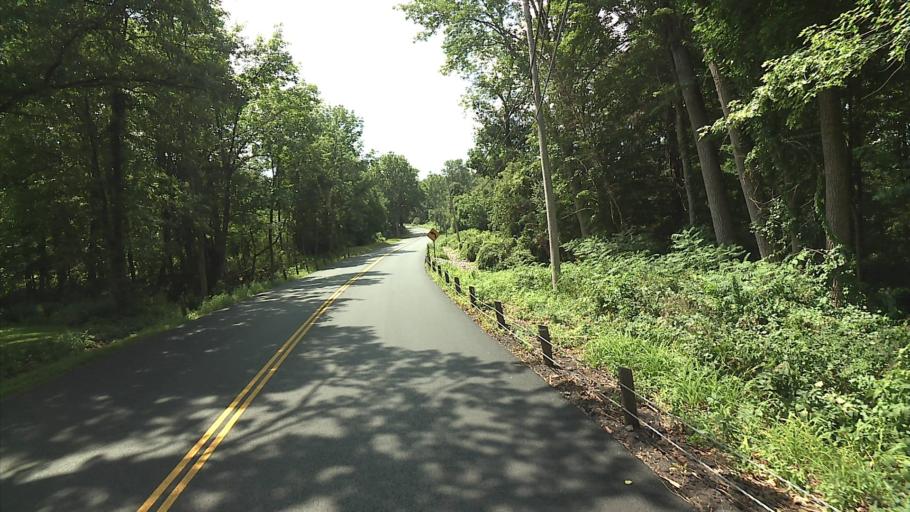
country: US
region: Connecticut
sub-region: Litchfield County
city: Canaan
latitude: 42.0013
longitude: -73.3575
